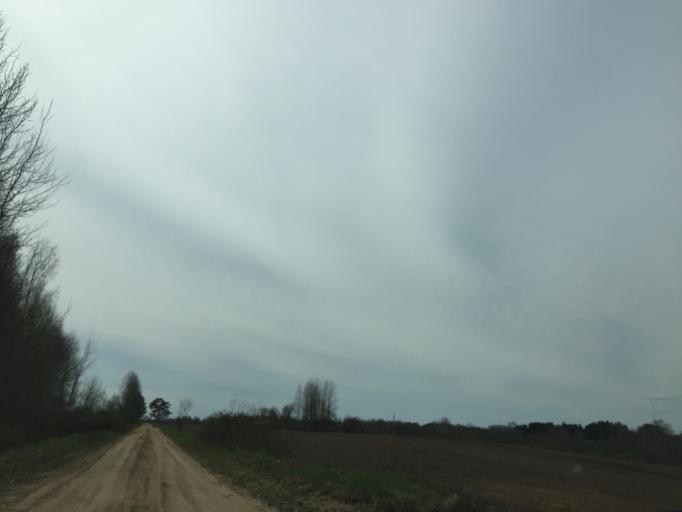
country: LV
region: Ludzas Rajons
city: Ludza
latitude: 56.5191
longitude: 27.5744
